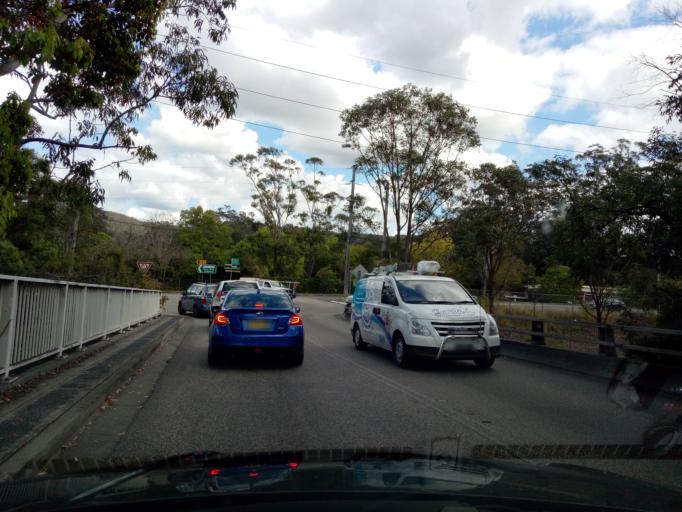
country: AU
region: New South Wales
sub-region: Gosford Shire
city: Narara
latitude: -33.3981
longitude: 151.3430
